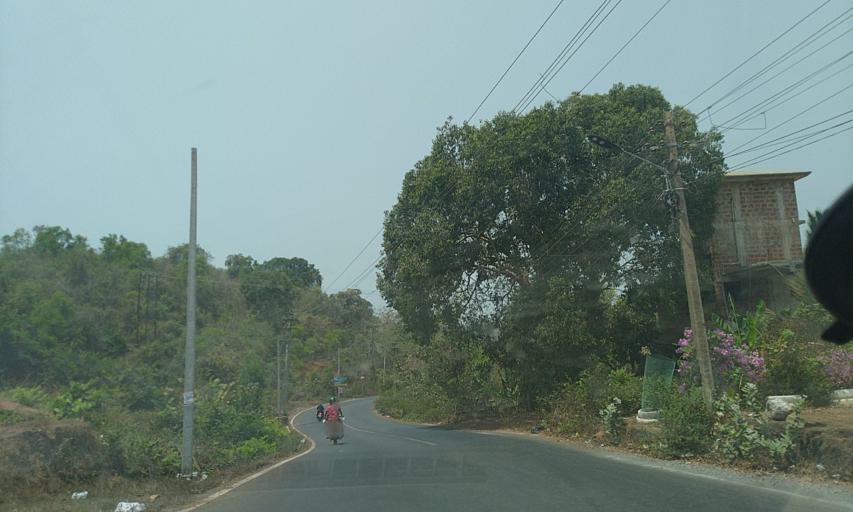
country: IN
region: Goa
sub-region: North Goa
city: Mapuca
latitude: 15.5954
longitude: 73.7951
